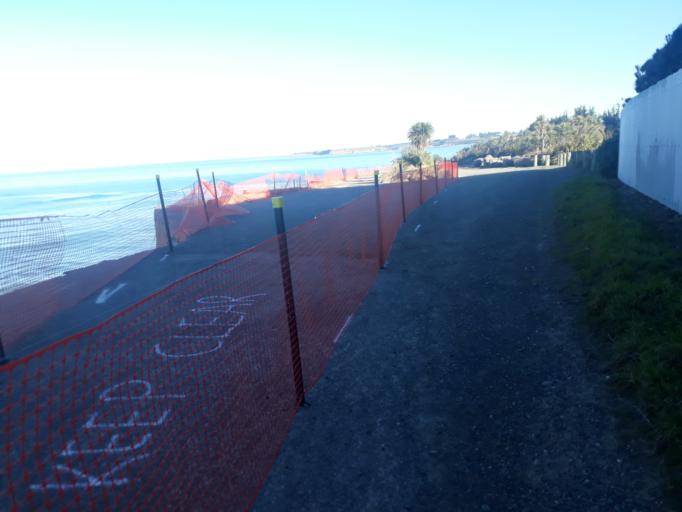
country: NZ
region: Canterbury
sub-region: Timaru District
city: Timaru
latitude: -44.4146
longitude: 171.2644
